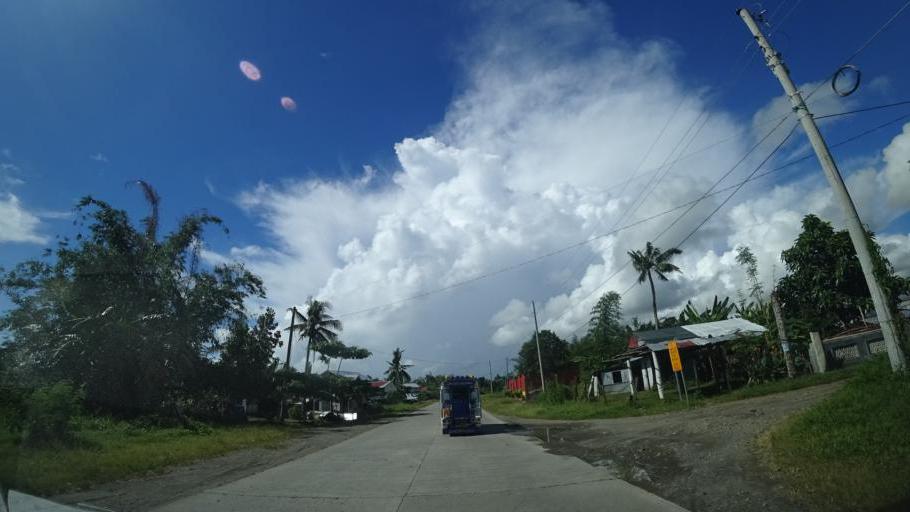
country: PH
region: Eastern Visayas
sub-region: Province of Leyte
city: Palo
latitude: 11.1560
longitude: 125.0015
